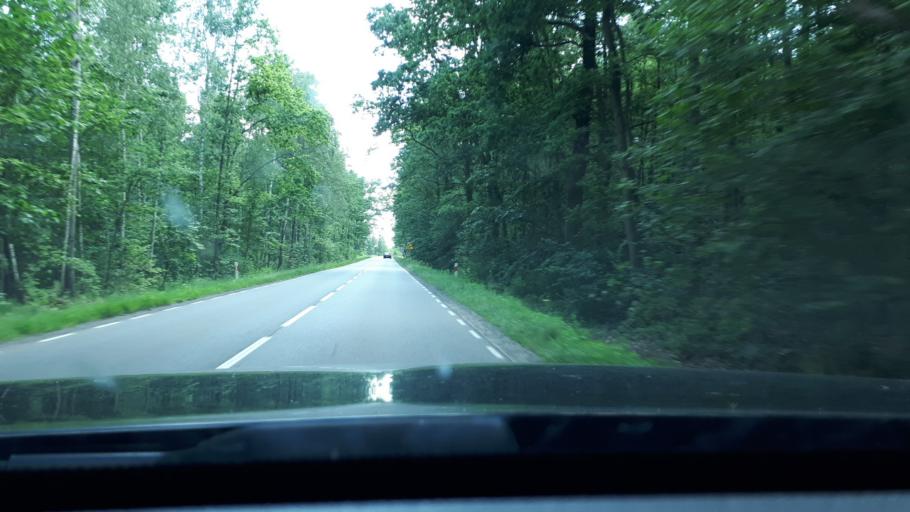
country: PL
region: Masovian Voivodeship
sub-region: Powiat piaseczynski
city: Gora Kalwaria
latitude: 51.8884
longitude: 21.2211
